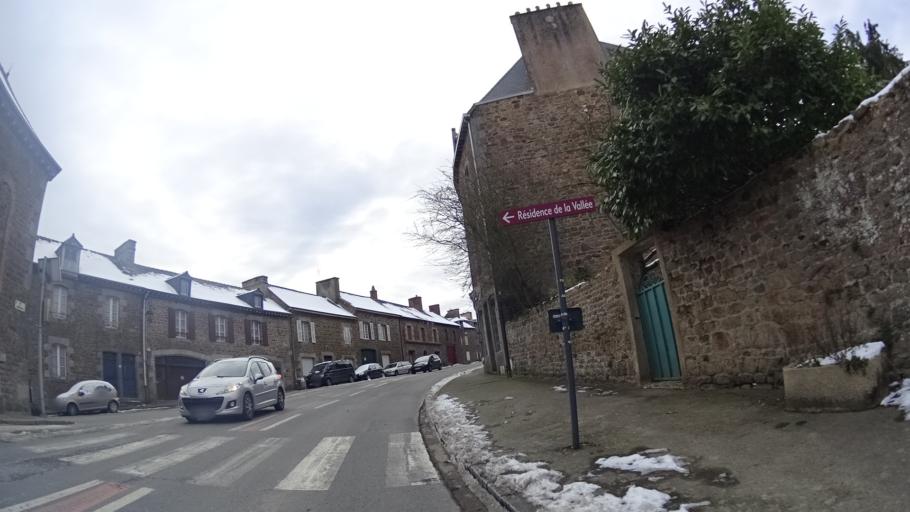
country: FR
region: Brittany
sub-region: Departement d'Ille-et-Vilaine
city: Irodouer
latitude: 48.2944
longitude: -1.9461
